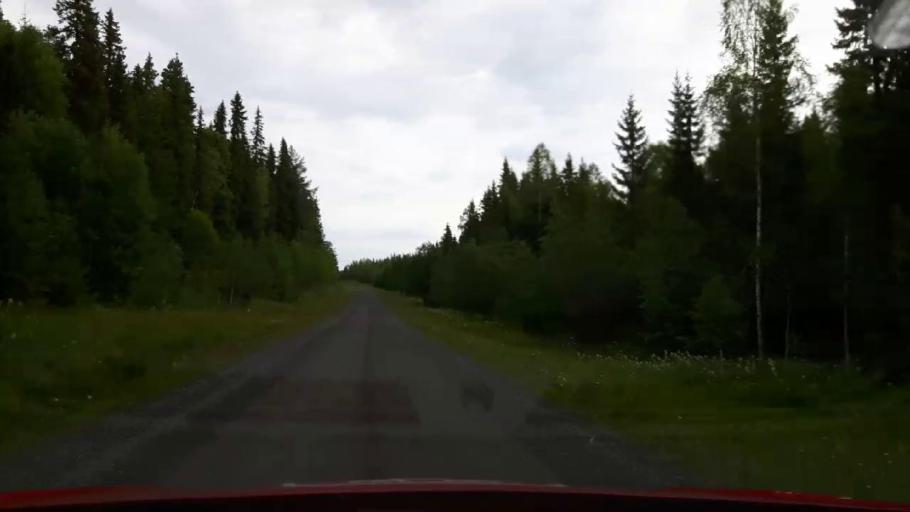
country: SE
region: Jaemtland
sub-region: OEstersunds Kommun
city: Lit
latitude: 63.3969
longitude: 15.2249
